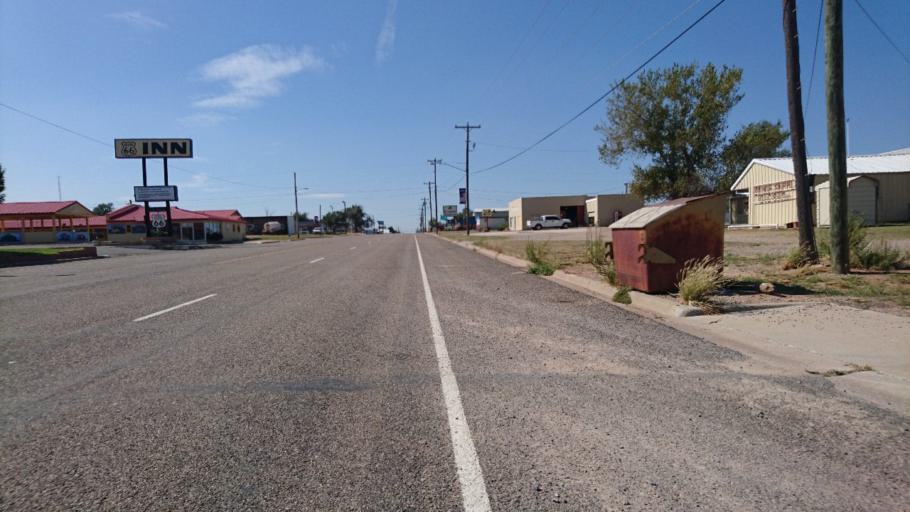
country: US
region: Texas
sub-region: Wheeler County
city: Shamrock
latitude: 35.2266
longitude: -100.2402
